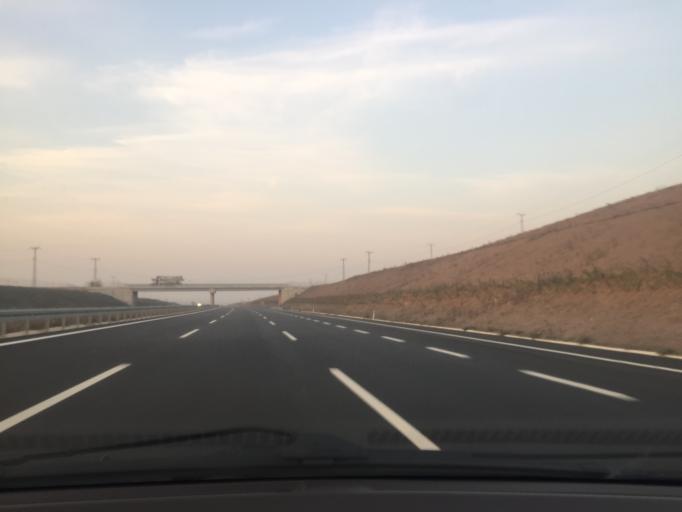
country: TR
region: Bursa
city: Karacabey
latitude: 40.2445
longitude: 28.4342
